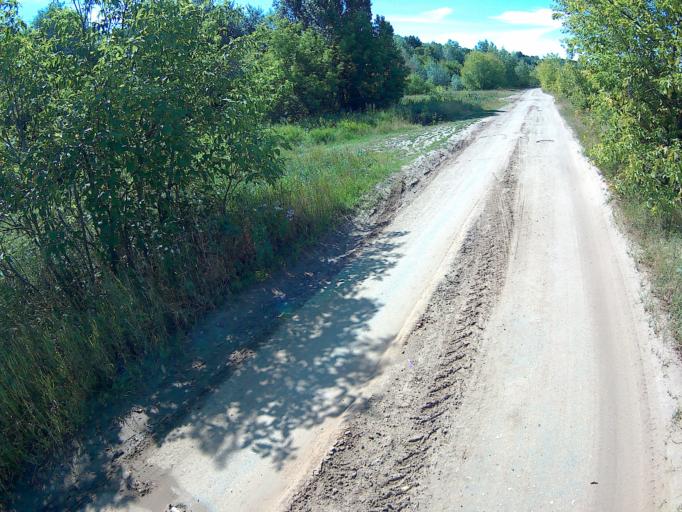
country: RU
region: Nizjnij Novgorod
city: Nizhniy Novgorod
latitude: 56.2580
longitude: 43.9650
